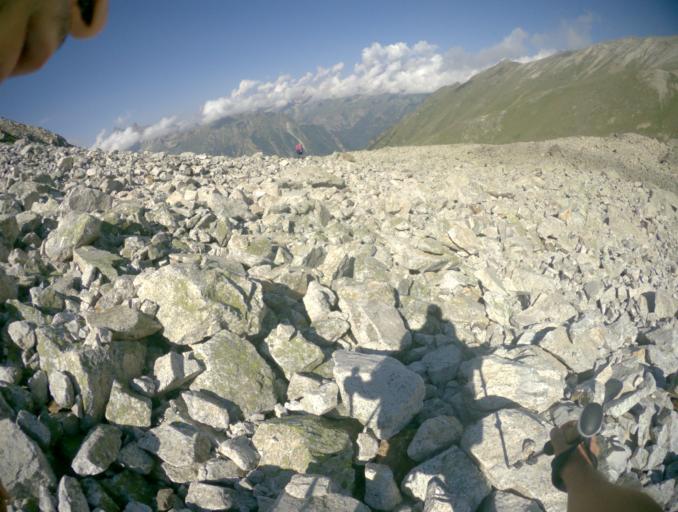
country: RU
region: Karachayevo-Cherkesiya
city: Uchkulan
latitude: 43.3069
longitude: 42.0643
